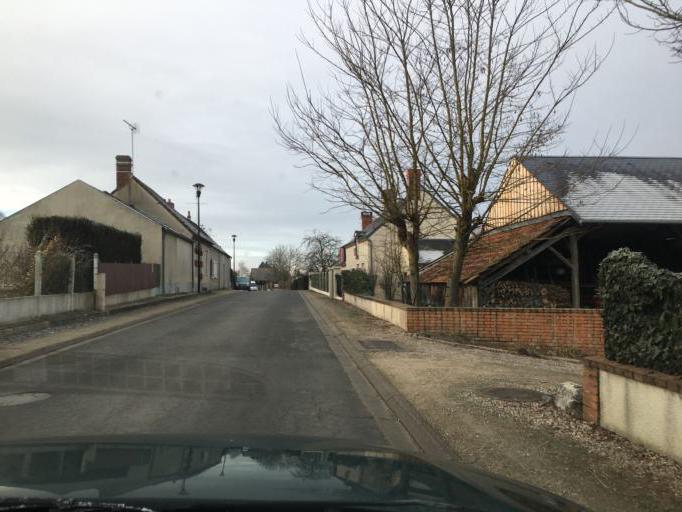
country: FR
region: Centre
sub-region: Departement du Loiret
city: Dry
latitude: 47.7959
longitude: 1.7123
